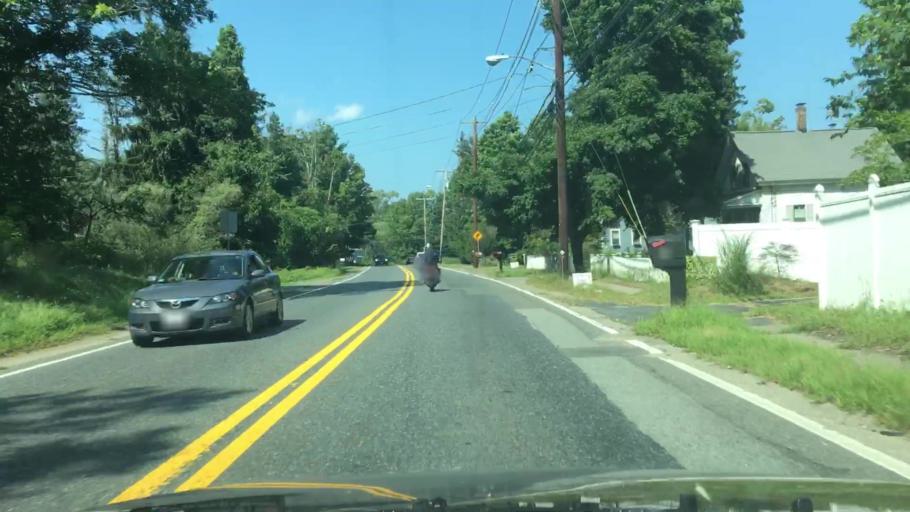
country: US
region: Massachusetts
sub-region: Middlesex County
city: Holliston
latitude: 42.1873
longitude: -71.4399
